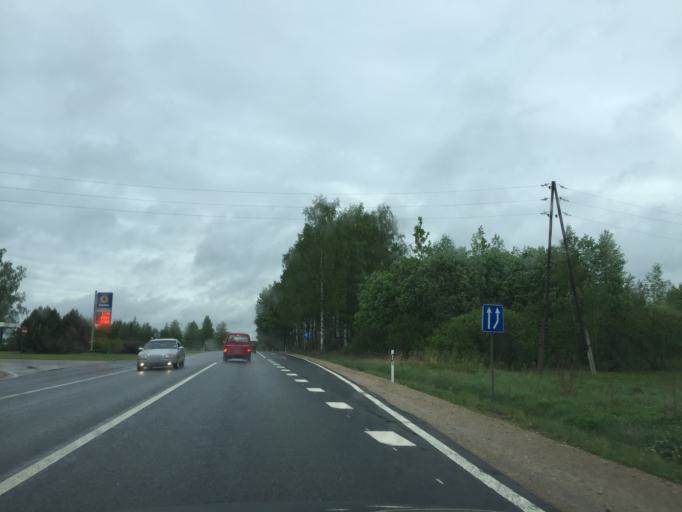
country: LV
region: Ogre
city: Jumprava
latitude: 56.6620
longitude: 24.8978
